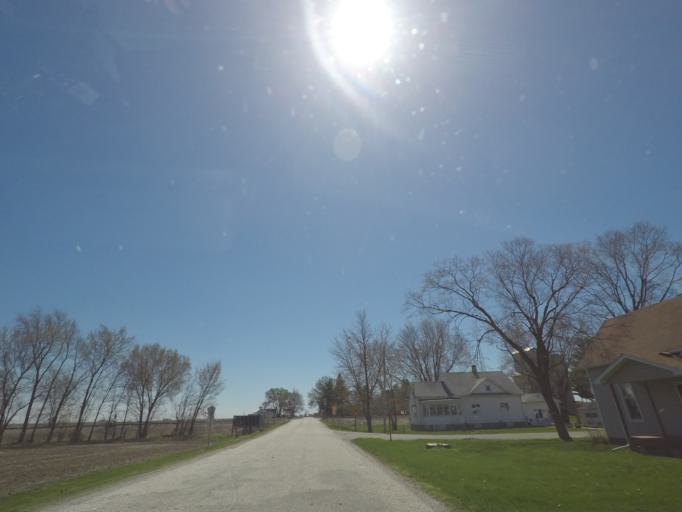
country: US
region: Illinois
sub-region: Logan County
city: Mount Pulaski
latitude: 40.0542
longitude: -89.1824
